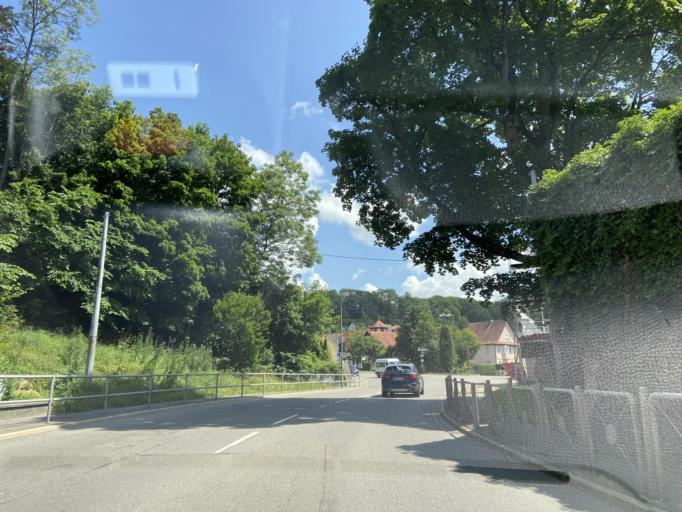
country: DE
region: Baden-Wuerttemberg
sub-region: Tuebingen Region
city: Messstetten
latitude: 48.2152
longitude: 8.9615
